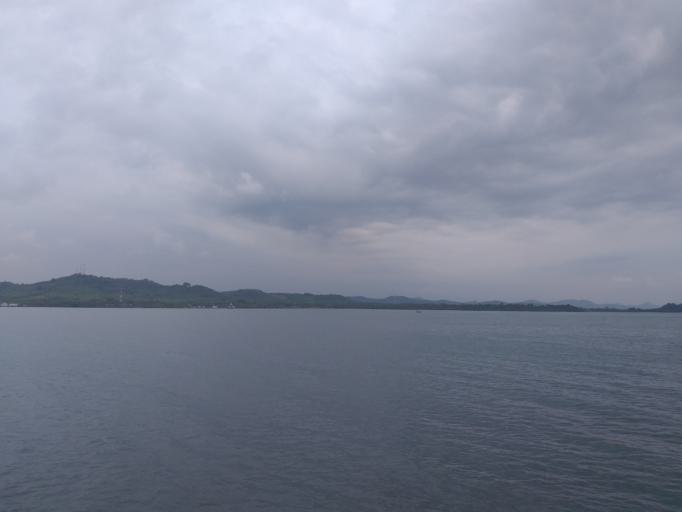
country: TH
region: Trat
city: Laem Ngop
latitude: 12.1682
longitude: 102.2957
